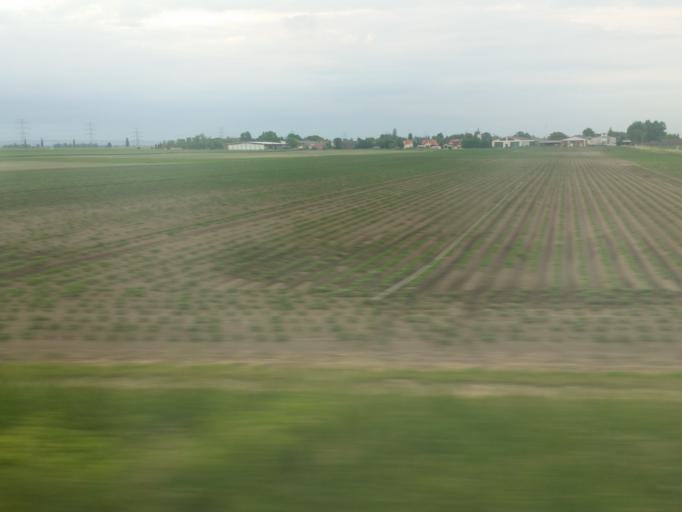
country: AT
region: Lower Austria
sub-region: Politischer Bezirk Ganserndorf
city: Raasdorf
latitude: 48.2382
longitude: 16.5638
